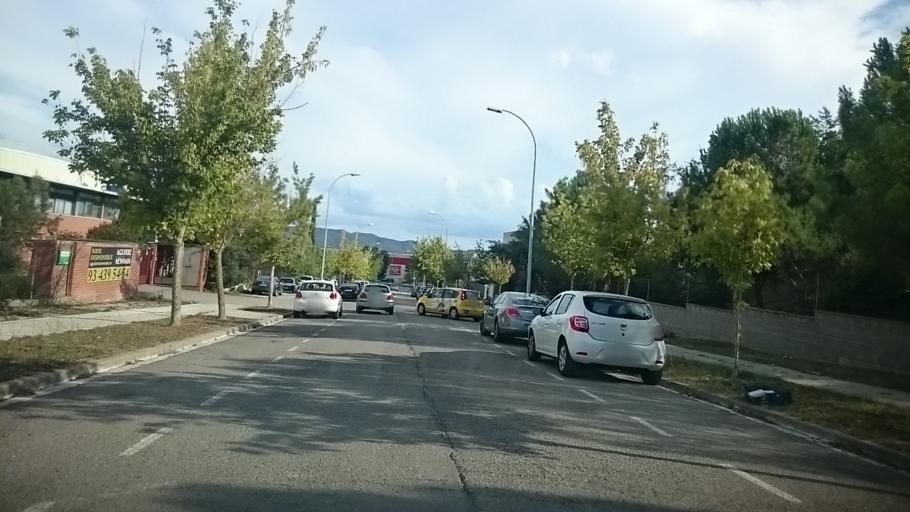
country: ES
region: Catalonia
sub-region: Provincia de Barcelona
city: Igualada
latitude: 41.5964
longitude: 1.6281
